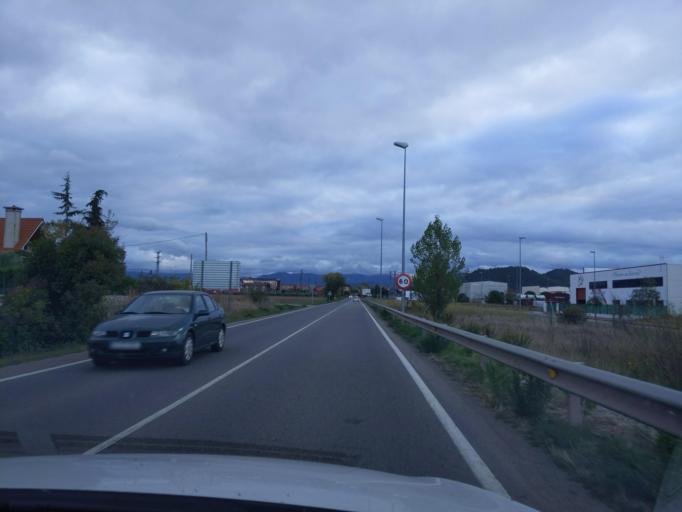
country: ES
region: La Rioja
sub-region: Provincia de La Rioja
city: Najera
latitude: 42.4272
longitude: -2.7191
